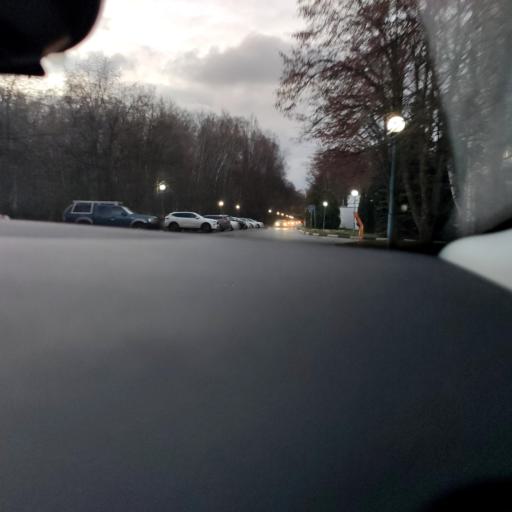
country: RU
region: Moscow
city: Babushkin
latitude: 55.8367
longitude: 37.7445
